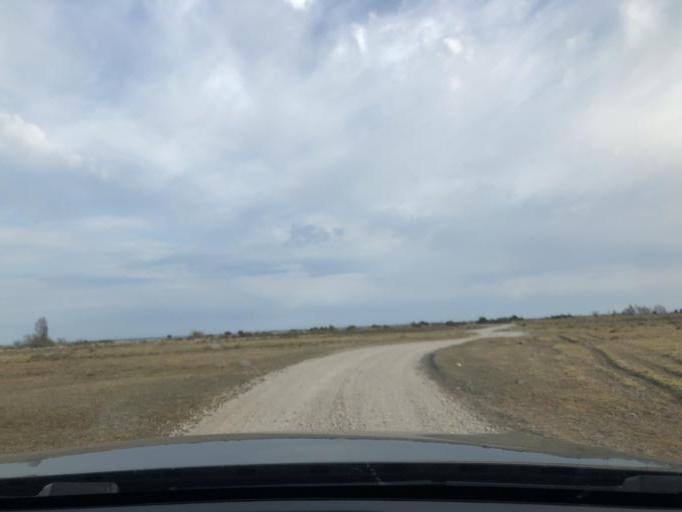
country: SE
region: Kalmar
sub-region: Morbylanga Kommun
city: Sodra Sandby
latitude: 56.5571
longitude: 16.6352
